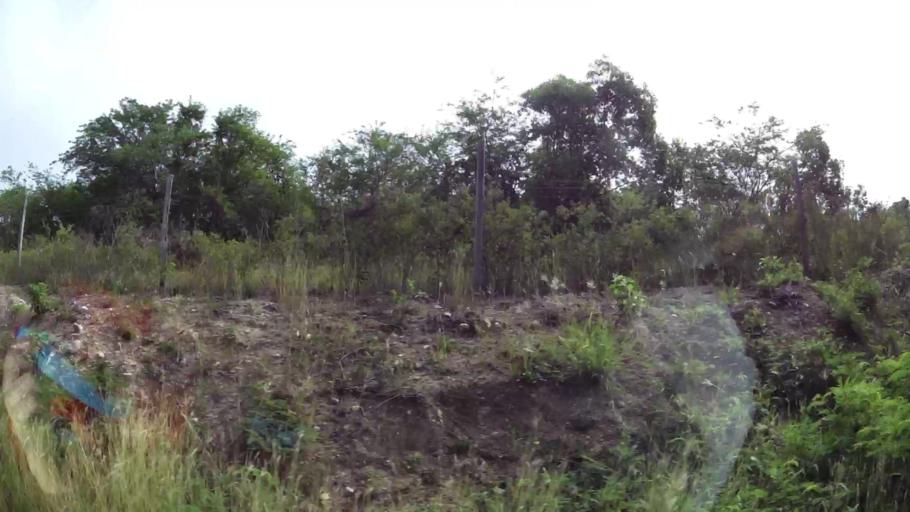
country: AG
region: Saint Paul
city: Liberta
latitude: 17.0484
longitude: -61.7285
